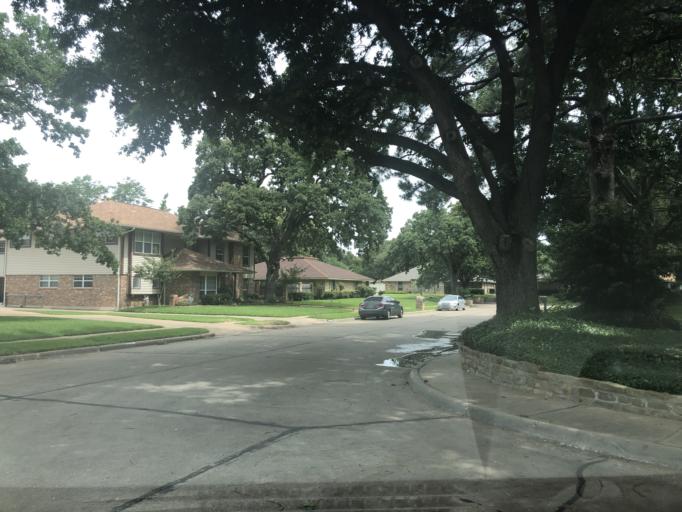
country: US
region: Texas
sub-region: Dallas County
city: Irving
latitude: 32.7982
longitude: -96.9827
